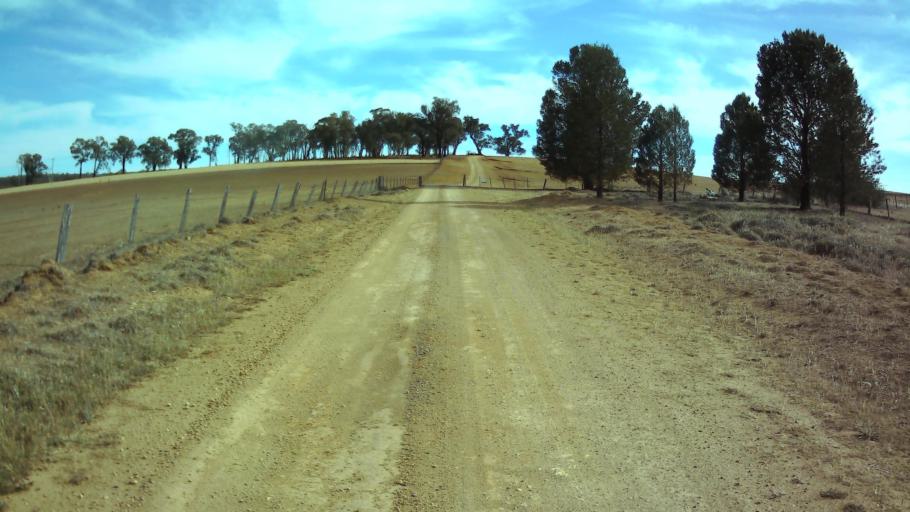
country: AU
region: New South Wales
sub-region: Weddin
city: Grenfell
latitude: -33.8969
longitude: 148.2037
